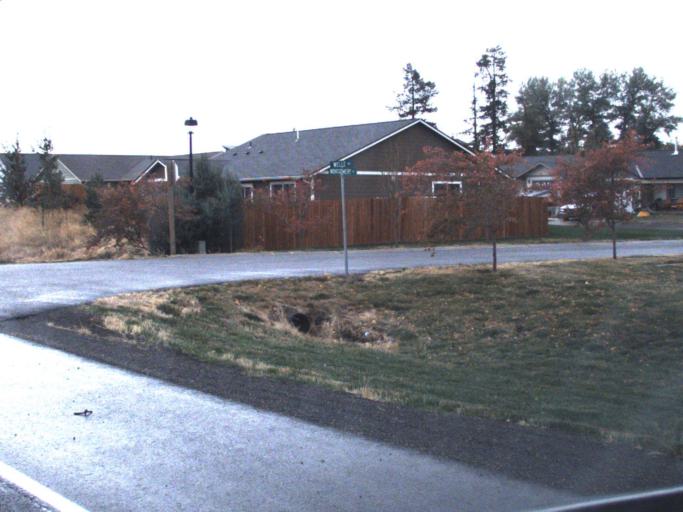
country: US
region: Washington
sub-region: Asotin County
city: Clarkston
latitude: 46.5330
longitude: -117.0858
